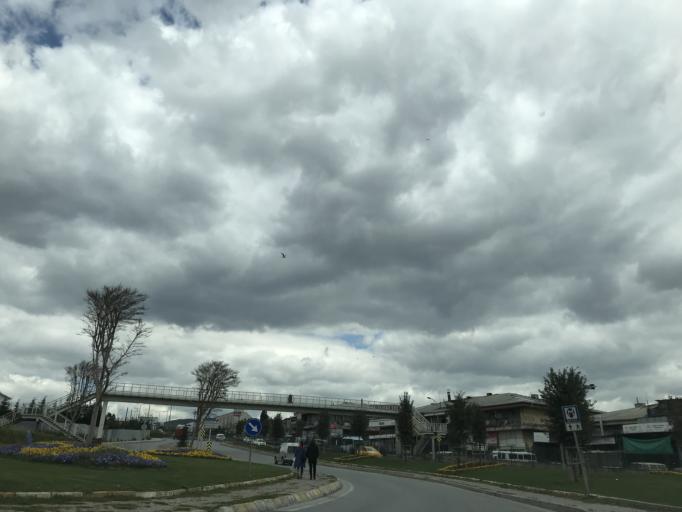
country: TR
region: Istanbul
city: Maltepe
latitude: 40.9005
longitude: 29.2060
